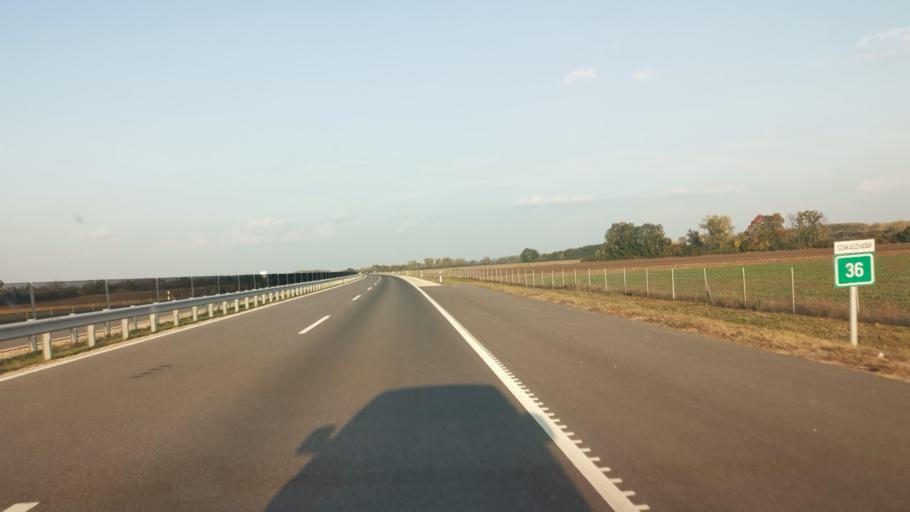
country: HU
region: Gyor-Moson-Sopron
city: Farad
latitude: 47.5689
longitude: 17.1417
